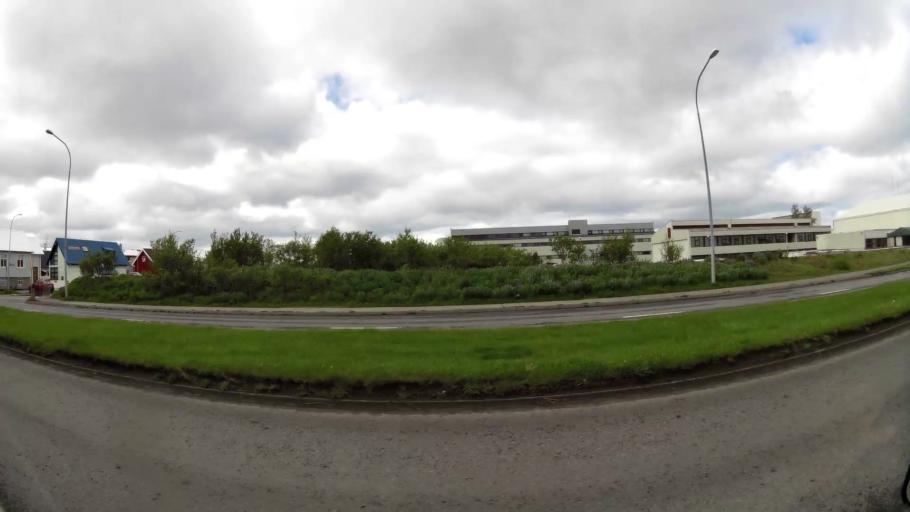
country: IS
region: Capital Region
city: Seltjarnarnes
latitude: 64.1381
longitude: -21.9534
